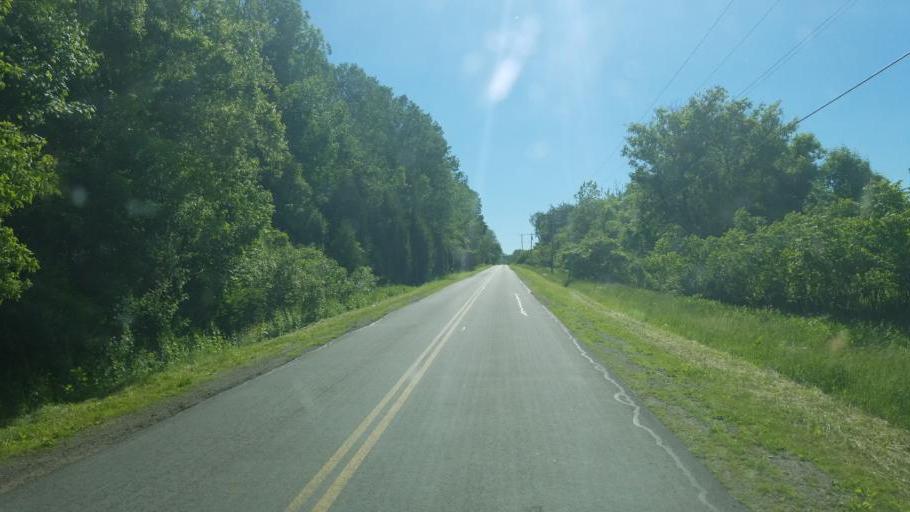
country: US
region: New York
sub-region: Montgomery County
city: Saint Johnsville
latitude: 42.9895
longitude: -74.7030
